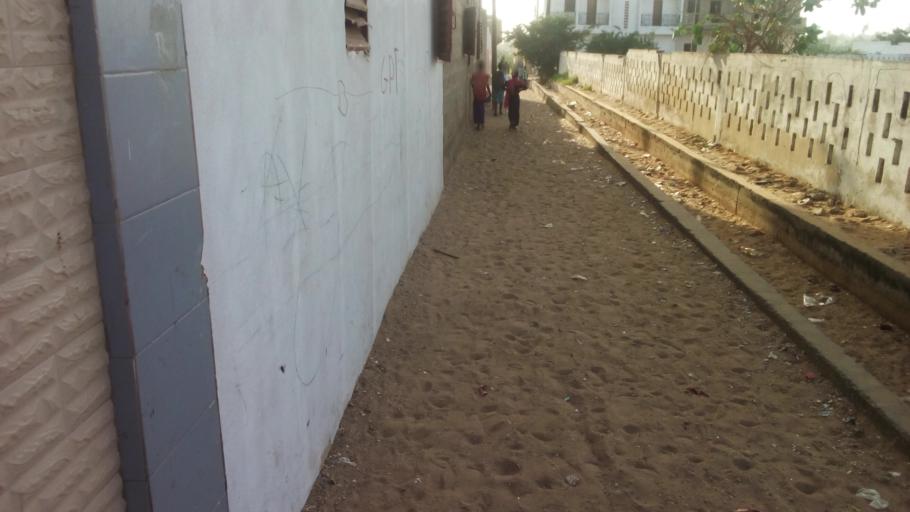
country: SN
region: Dakar
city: Pikine
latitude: 14.7962
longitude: -17.3365
